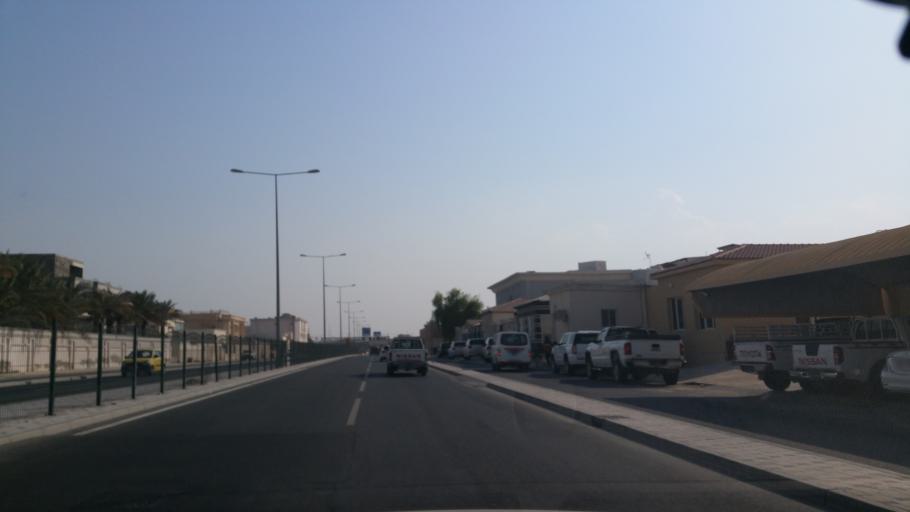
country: QA
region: Baladiyat ar Rayyan
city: Ar Rayyan
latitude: 25.3156
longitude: 51.4082
